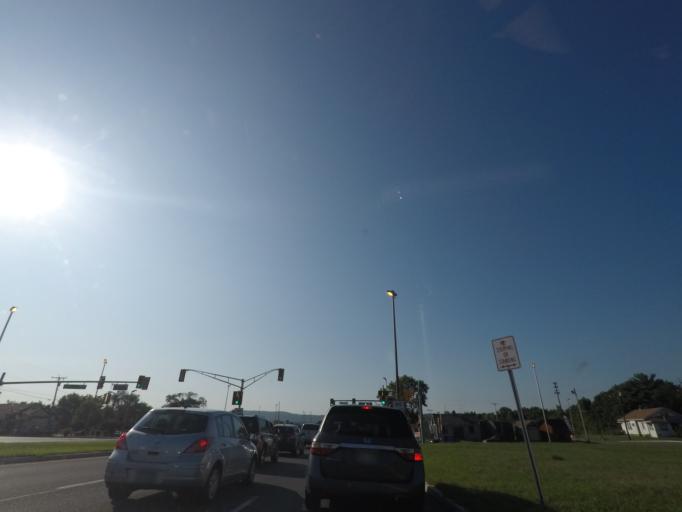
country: US
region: New Jersey
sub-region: Warren County
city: Alpha
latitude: 40.6738
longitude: -75.1391
